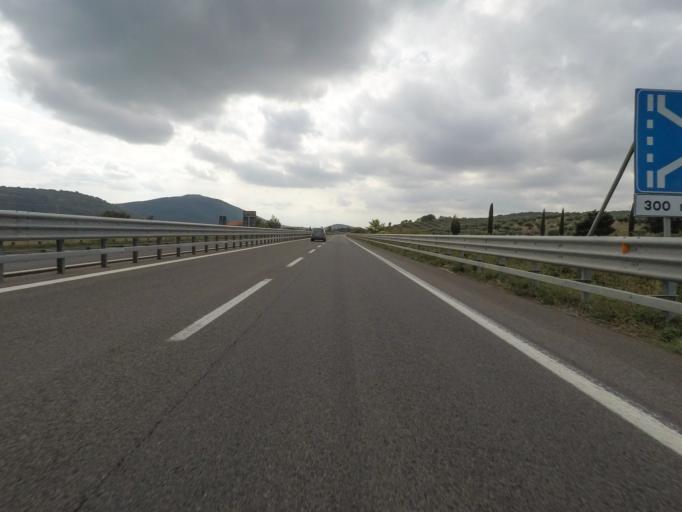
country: IT
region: Tuscany
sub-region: Provincia di Grosseto
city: Bagno Roselle
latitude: 42.8431
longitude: 11.1543
